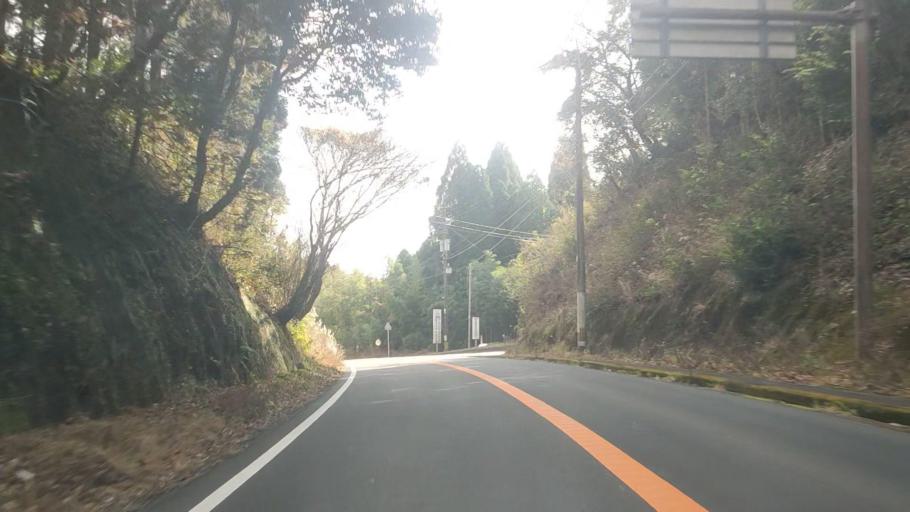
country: JP
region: Kagoshima
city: Kajiki
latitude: 31.8268
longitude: 130.6889
